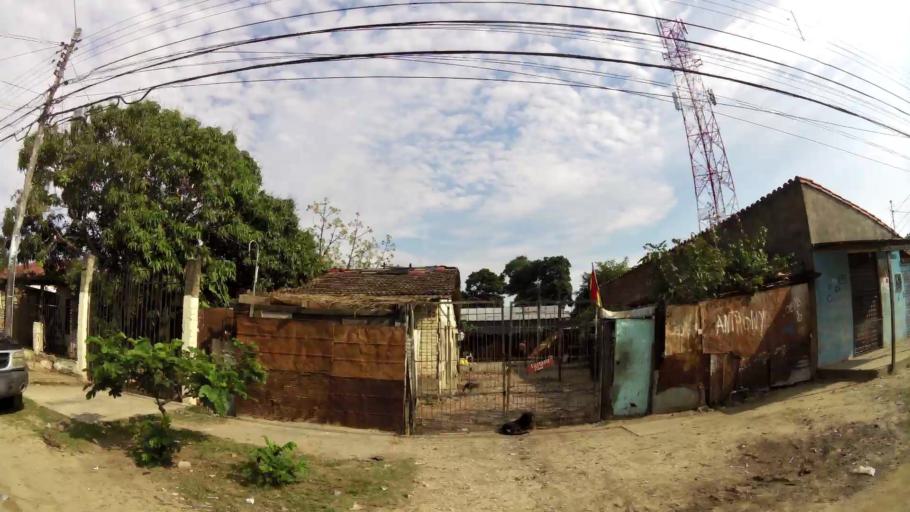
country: BO
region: Santa Cruz
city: Santa Cruz de la Sierra
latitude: -17.7339
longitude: -63.1421
